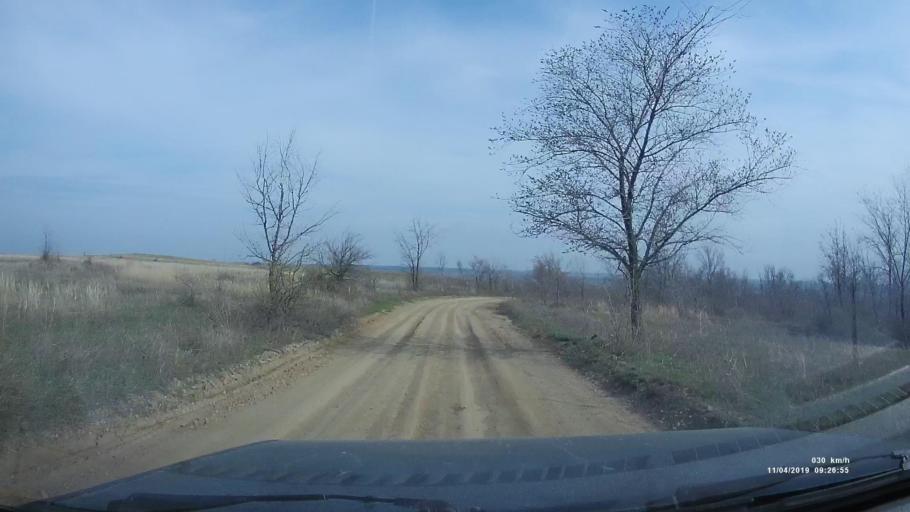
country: RU
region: Rostov
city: Staraya Stanitsa
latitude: 48.2644
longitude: 40.3650
